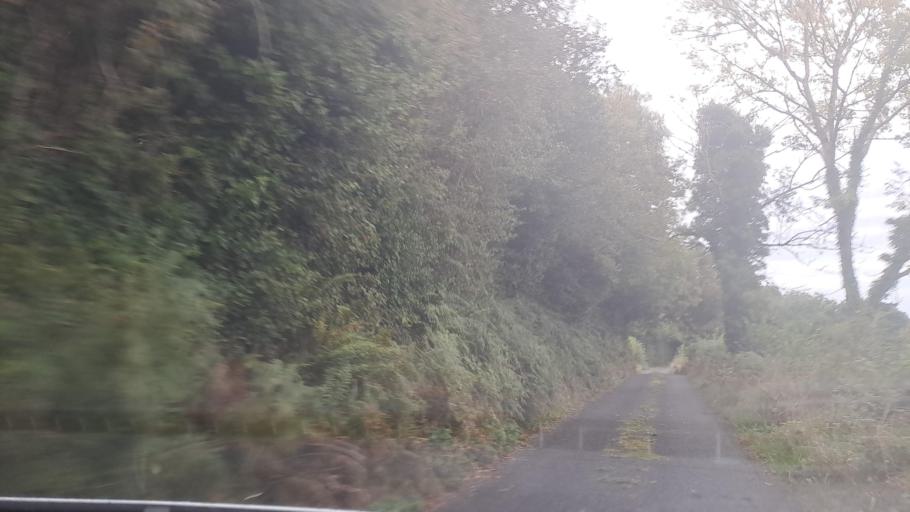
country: IE
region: Ulster
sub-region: County Monaghan
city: Carrickmacross
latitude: 53.9850
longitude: -6.7915
